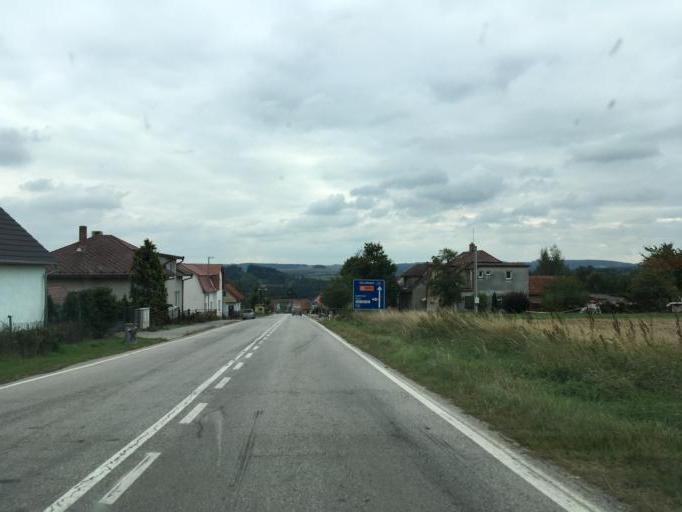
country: CZ
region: Vysocina
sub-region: Okres Pelhrimov
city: Zeliv
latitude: 49.5388
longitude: 15.1658
